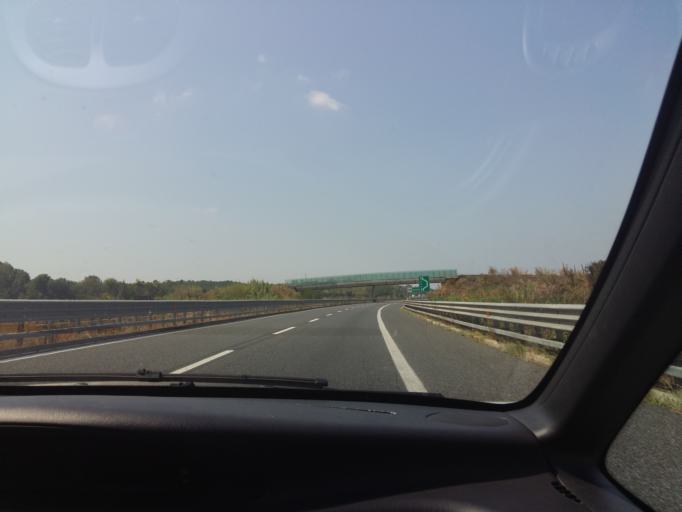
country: IT
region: Calabria
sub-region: Provincia di Reggio Calabria
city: Rosarno
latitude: 38.5009
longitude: 16.0295
